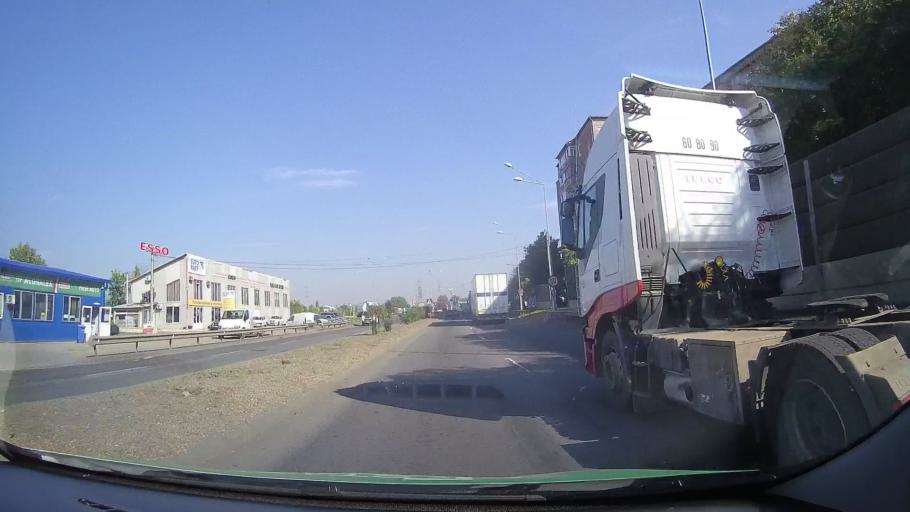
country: RO
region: Bihor
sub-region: Comuna Biharea
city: Oradea
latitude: 47.0677
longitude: 21.9009
